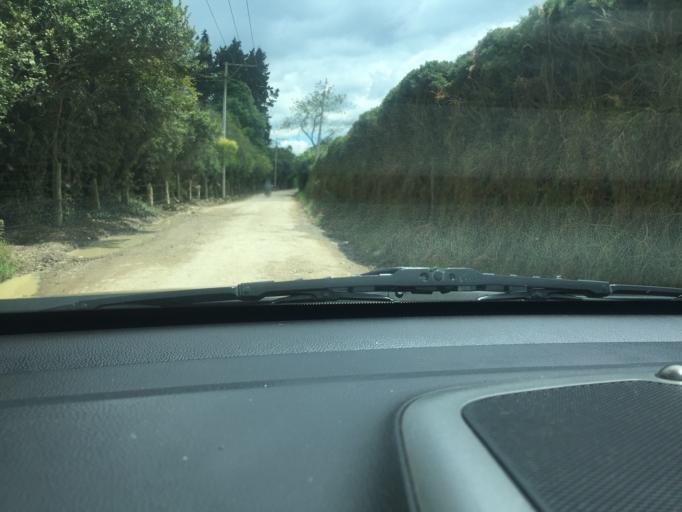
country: CO
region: Cundinamarca
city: Facatativa
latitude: 4.7941
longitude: -74.3200
